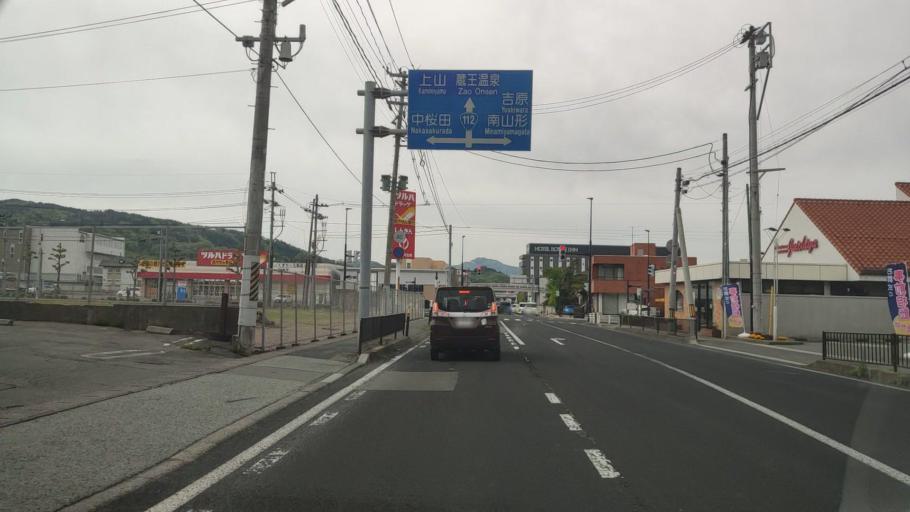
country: JP
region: Yamagata
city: Yamagata-shi
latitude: 38.2191
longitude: 140.3241
